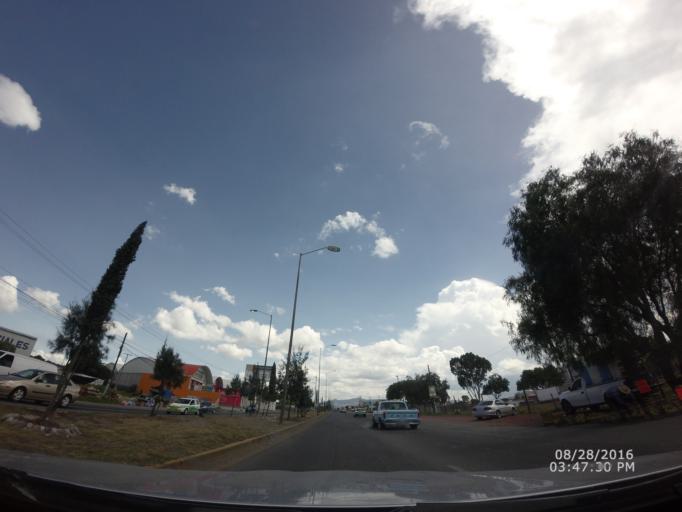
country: MX
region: Hidalgo
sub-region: Mineral de la Reforma
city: Nuevo Centro de Poblacion Agricola el Chacon
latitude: 20.0657
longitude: -98.7443
